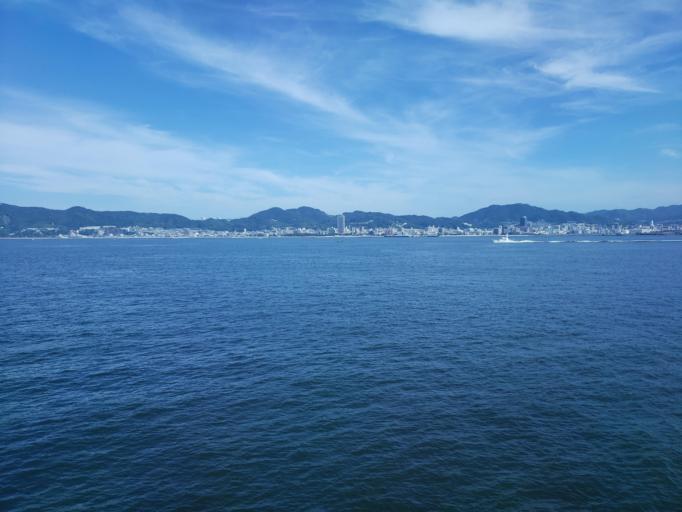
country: JP
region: Hyogo
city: Kobe
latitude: 34.6212
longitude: 135.1390
